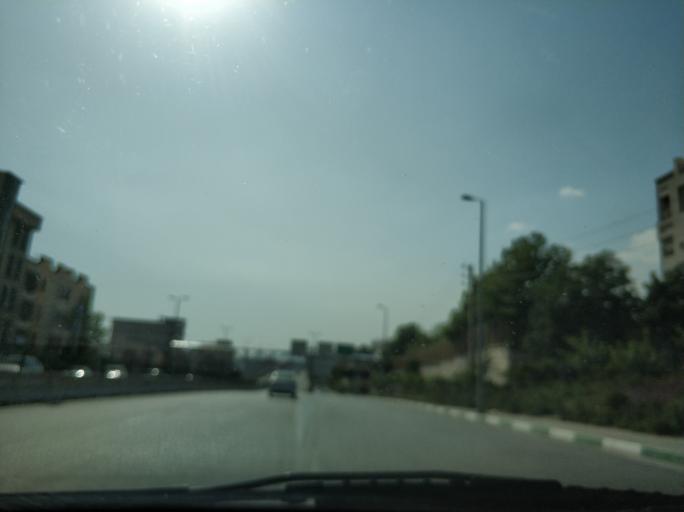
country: IR
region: Tehran
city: Tajrish
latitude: 35.7585
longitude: 51.5398
